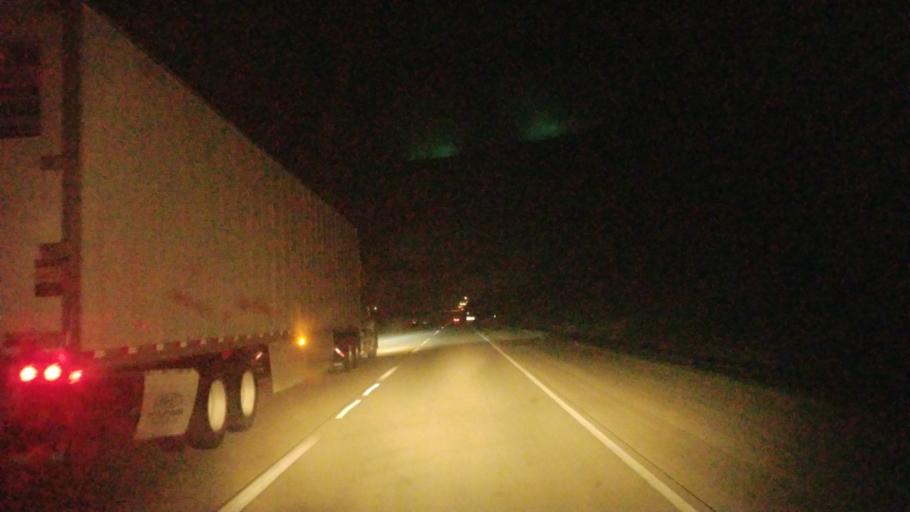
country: US
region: Illinois
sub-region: Clark County
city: Marshall
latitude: 39.4219
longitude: -87.6374
